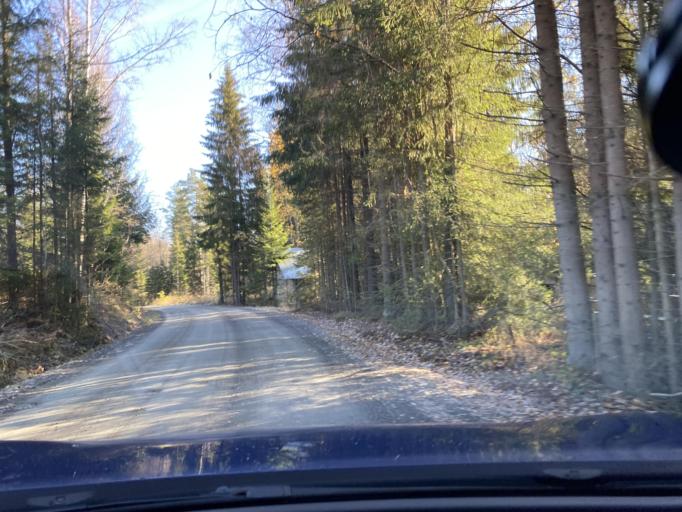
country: FI
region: Haeme
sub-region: Haemeenlinna
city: Kalvola
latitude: 60.9865
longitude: 24.0593
